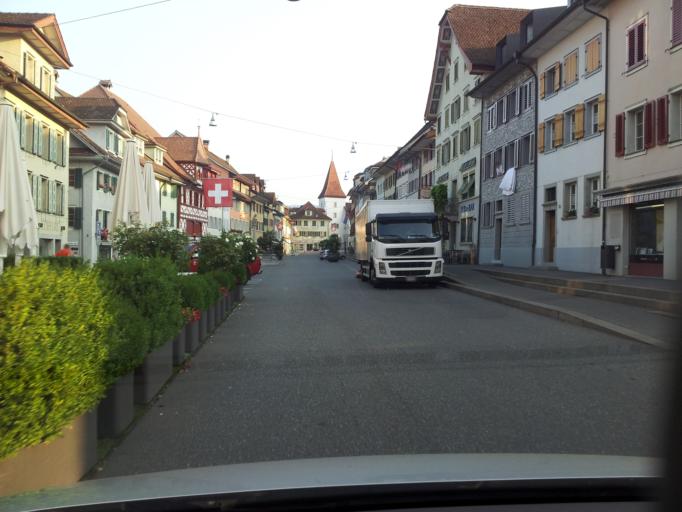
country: CH
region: Lucerne
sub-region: Sursee District
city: Sempach
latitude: 47.1353
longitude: 8.1916
